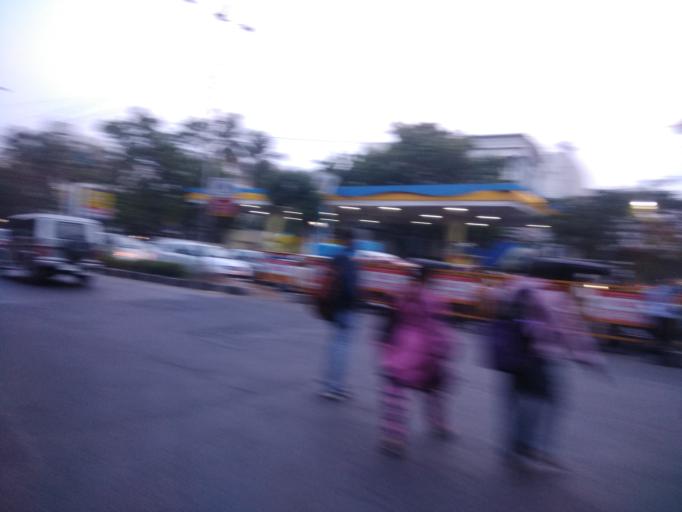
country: IN
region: Tamil Nadu
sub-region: Kancheepuram
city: Alandur
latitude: 13.0113
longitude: 80.2233
